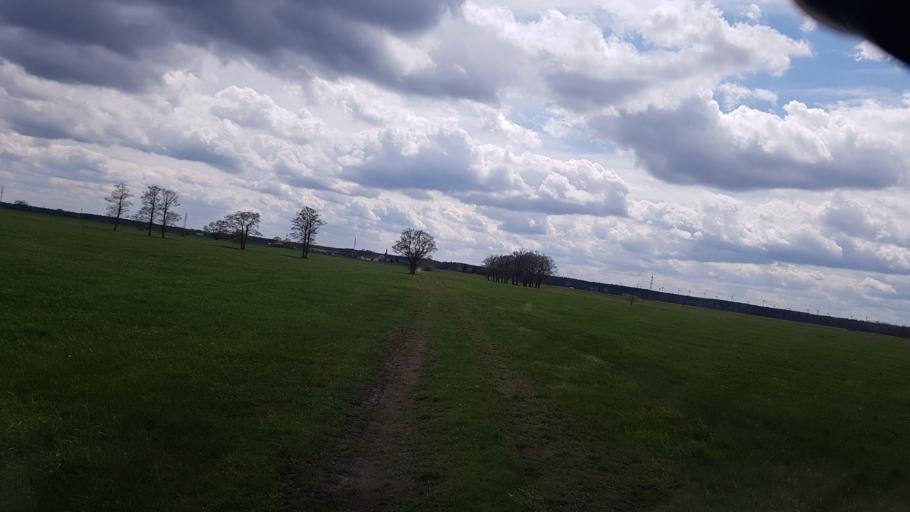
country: DE
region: Brandenburg
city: Bronkow
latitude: 51.6063
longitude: 13.9293
